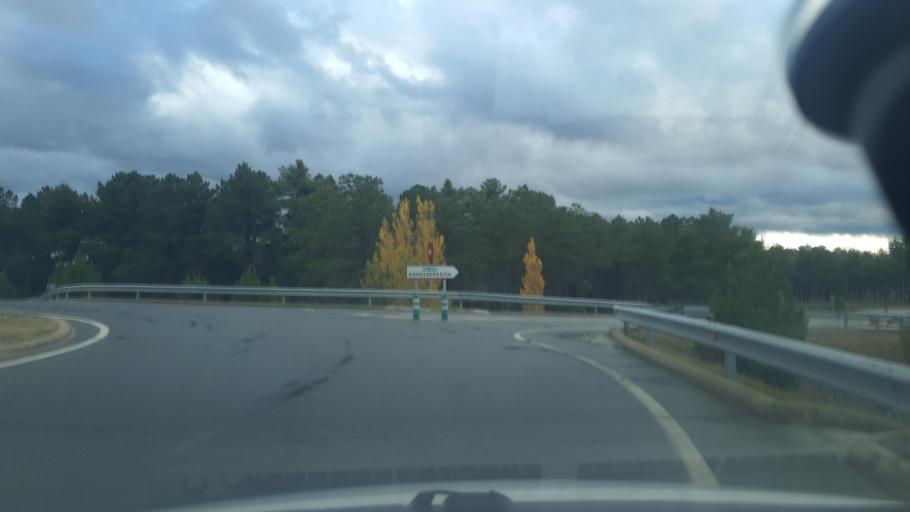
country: ES
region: Castille and Leon
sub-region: Provincia de Segovia
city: Sanchonuno
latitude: 41.2945
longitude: -4.3017
